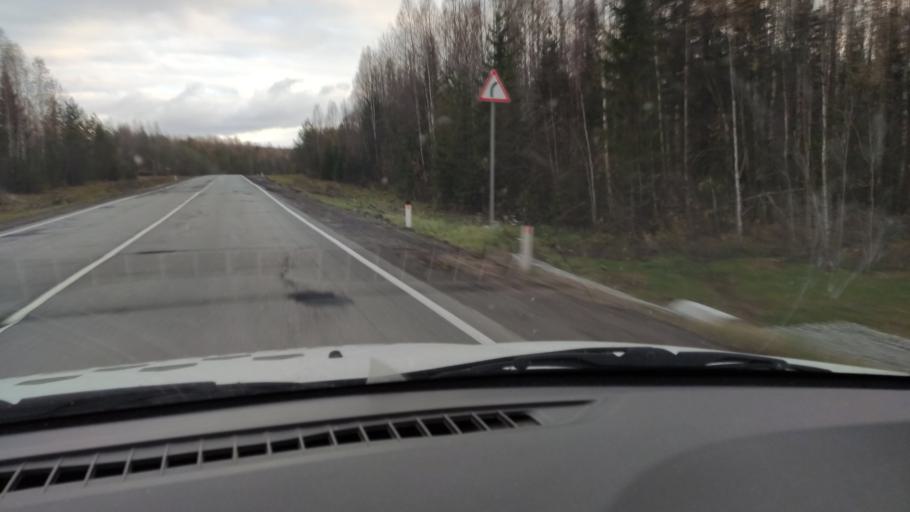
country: RU
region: Kirov
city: Omutninsk
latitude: 58.7519
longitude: 52.0527
